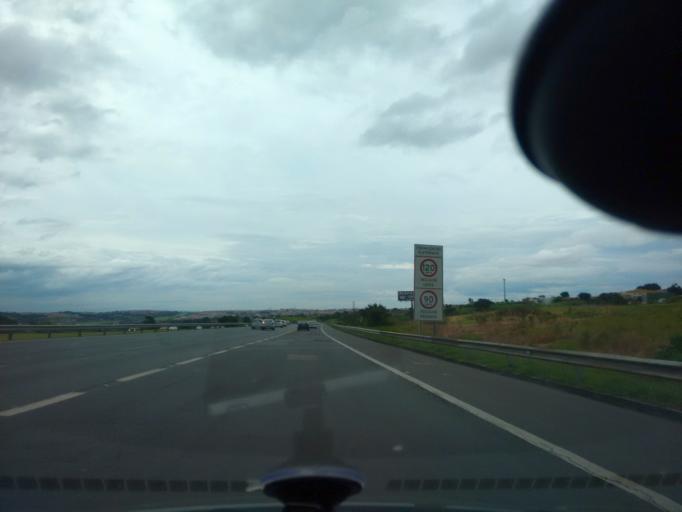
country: BR
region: Sao Paulo
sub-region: Campinas
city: Campinas
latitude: -22.9854
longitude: -47.1112
